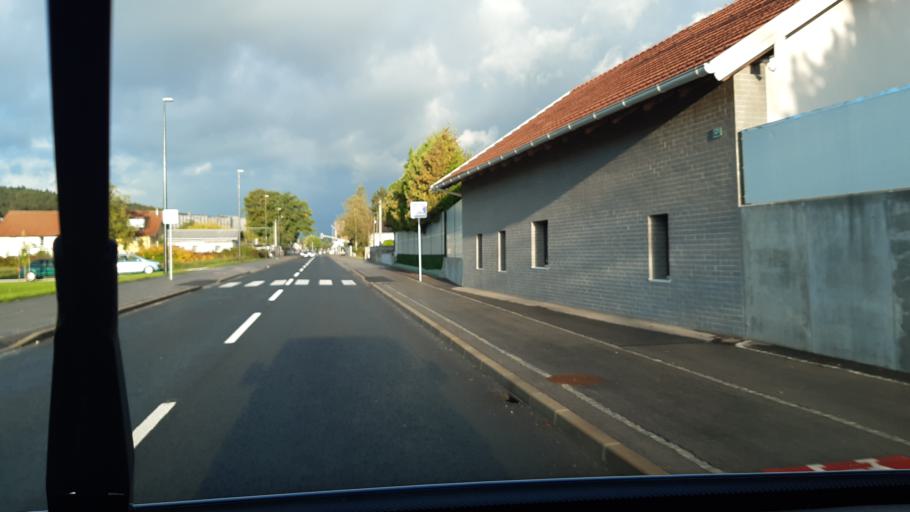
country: SI
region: Skofljica
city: Lavrica
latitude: 46.0461
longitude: 14.5563
